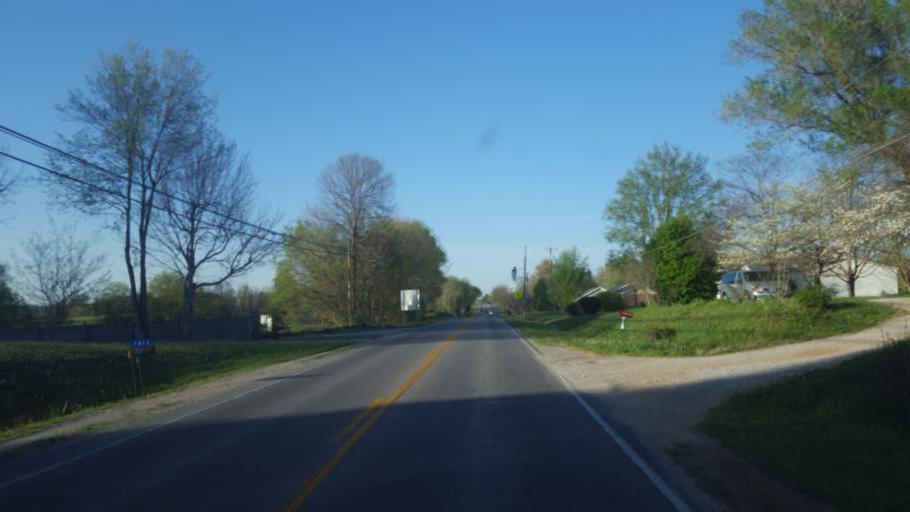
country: US
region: Kentucky
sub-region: Hart County
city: Munfordville
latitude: 37.2566
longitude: -85.8856
